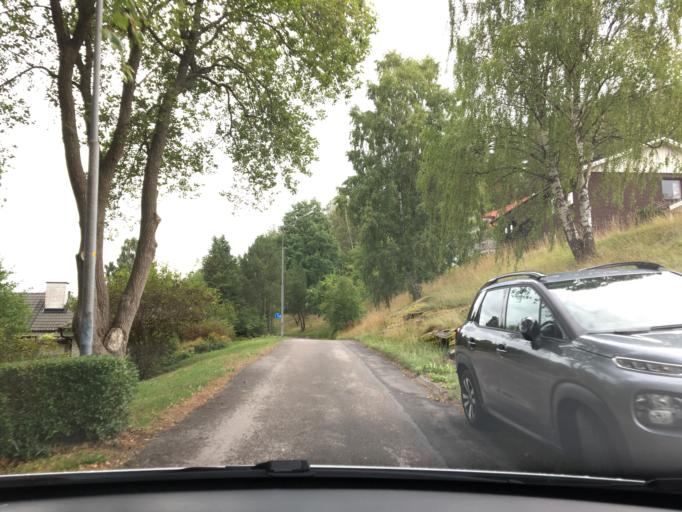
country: SE
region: Vaestra Goetaland
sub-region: Ale Kommun
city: Nodinge-Nol
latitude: 57.8935
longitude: 12.0621
